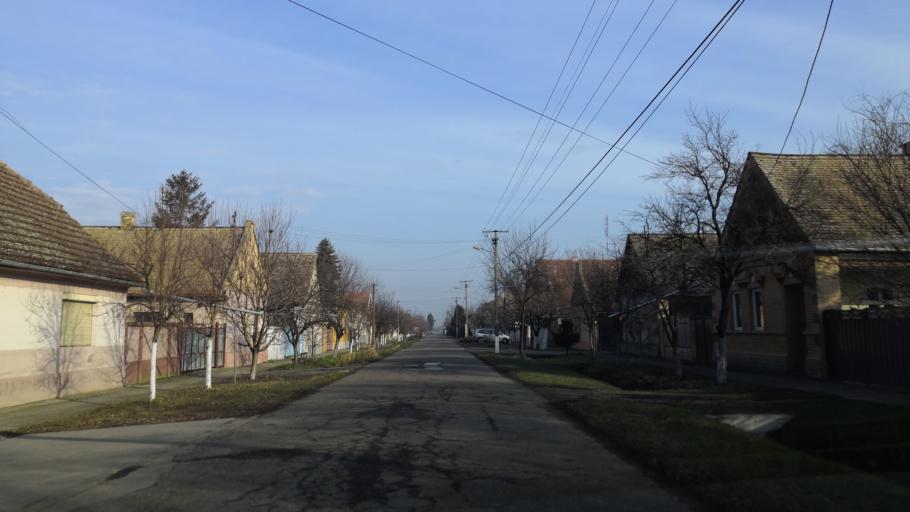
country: RS
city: Kisac
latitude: 45.3471
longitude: 19.7323
